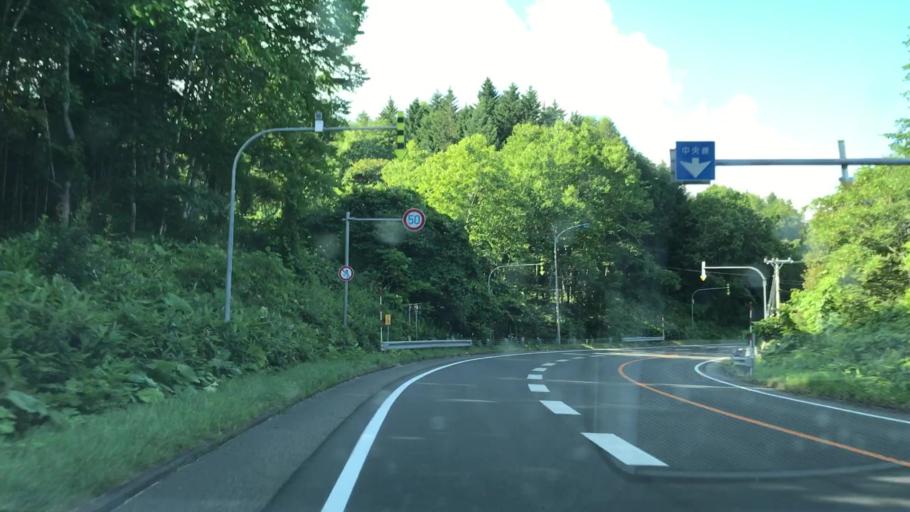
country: JP
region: Hokkaido
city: Shimo-furano
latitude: 42.9013
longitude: 142.4209
